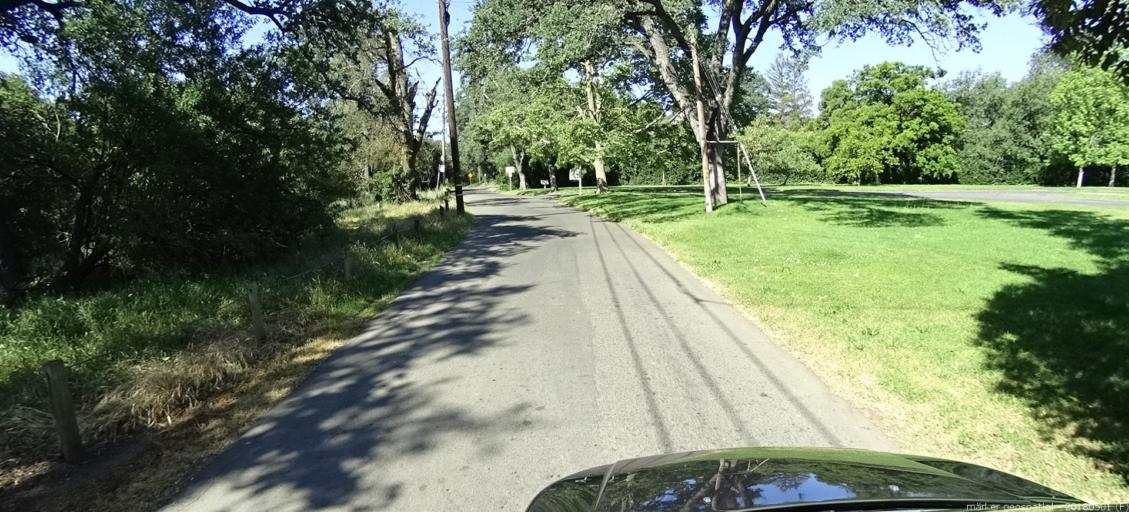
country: US
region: California
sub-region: Sacramento County
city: Arden-Arcade
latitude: 38.6432
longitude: -121.3757
